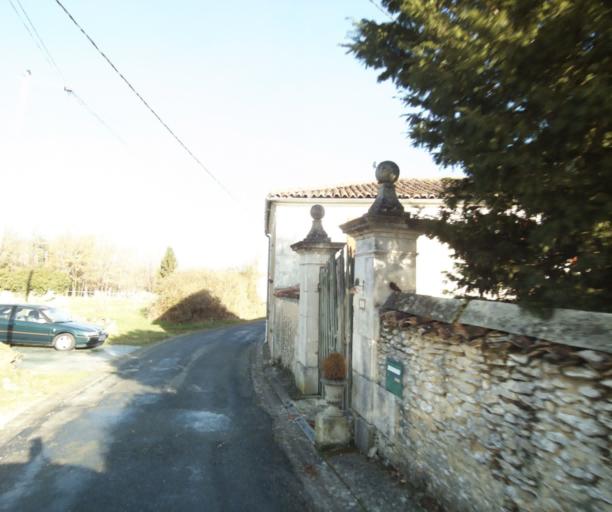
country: FR
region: Poitou-Charentes
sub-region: Departement de la Charente-Maritime
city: Burie
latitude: 45.7570
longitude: -0.4840
